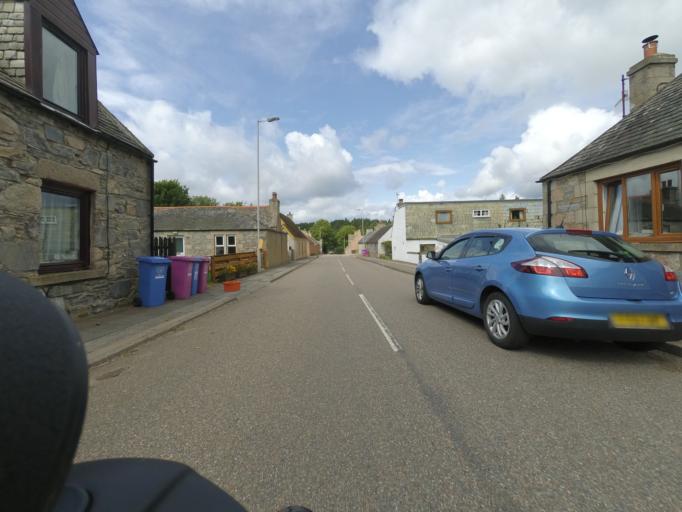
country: GB
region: Scotland
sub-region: Highland
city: Grantown on Spey
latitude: 57.2554
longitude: -3.3842
